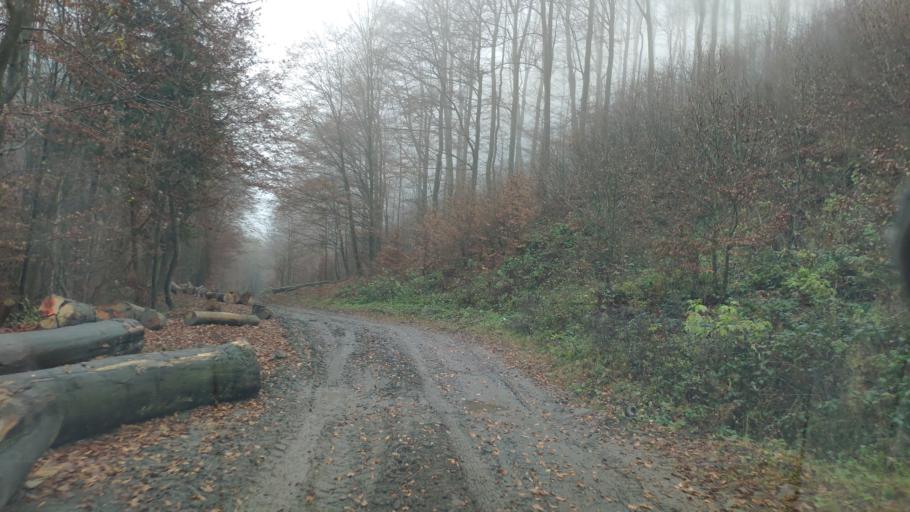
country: SK
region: Presovsky
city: Sabinov
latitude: 49.1597
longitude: 21.1984
